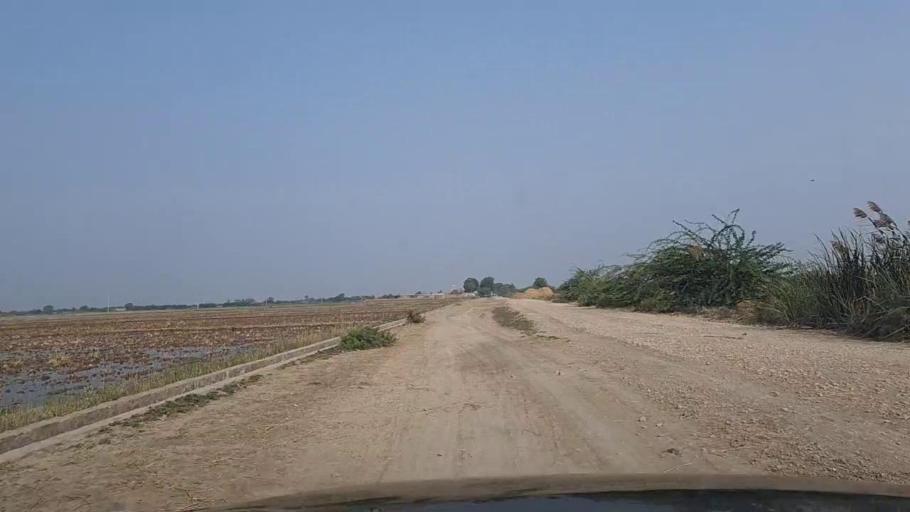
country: PK
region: Sindh
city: Thatta
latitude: 24.7630
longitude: 67.8713
